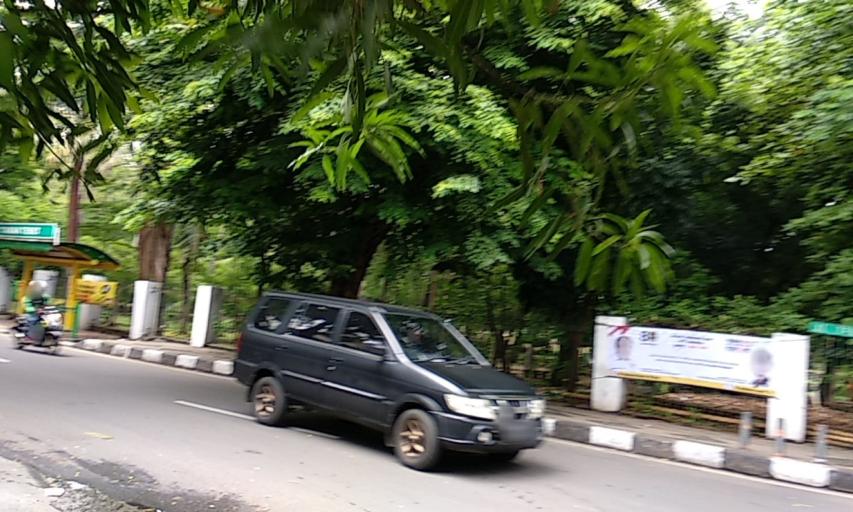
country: ID
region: Jakarta Raya
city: Jakarta
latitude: -6.2379
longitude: 106.8535
